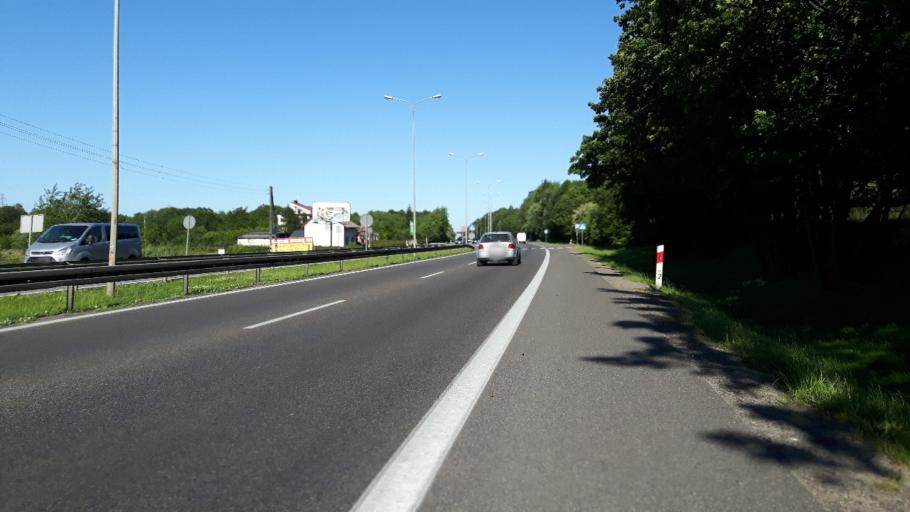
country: PL
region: Pomeranian Voivodeship
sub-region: Powiat wejherowski
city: Reda
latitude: 54.6041
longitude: 18.3270
